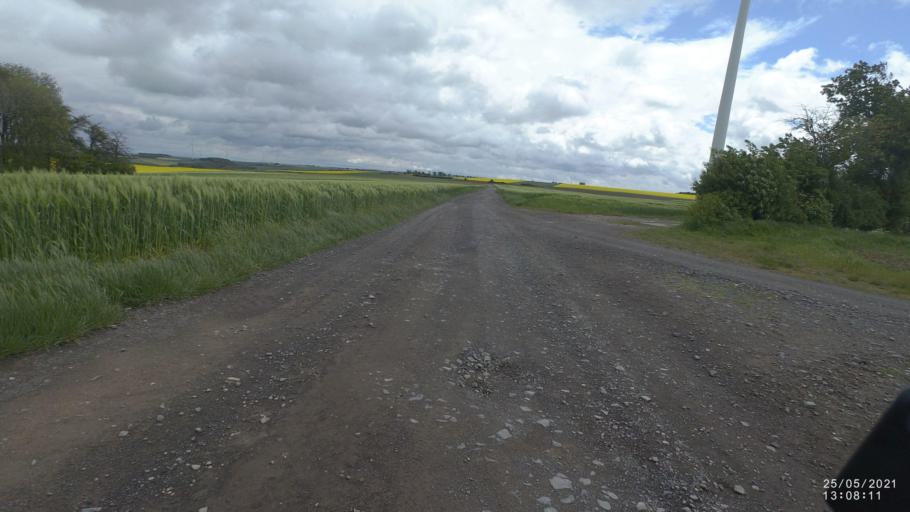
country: DE
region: Rheinland-Pfalz
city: Kehrig
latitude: 50.2959
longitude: 7.2065
